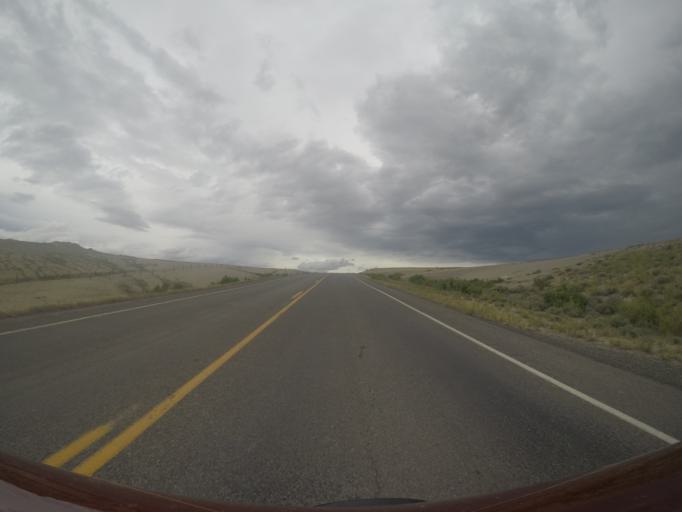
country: US
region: Wyoming
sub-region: Big Horn County
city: Lovell
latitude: 44.8864
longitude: -108.2890
